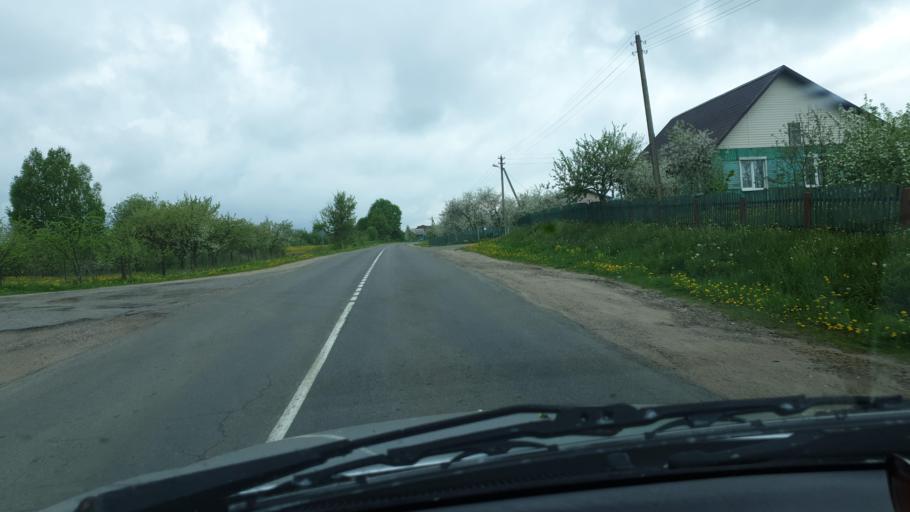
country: BY
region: Vitebsk
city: Lyepyel'
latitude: 54.8863
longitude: 28.6306
